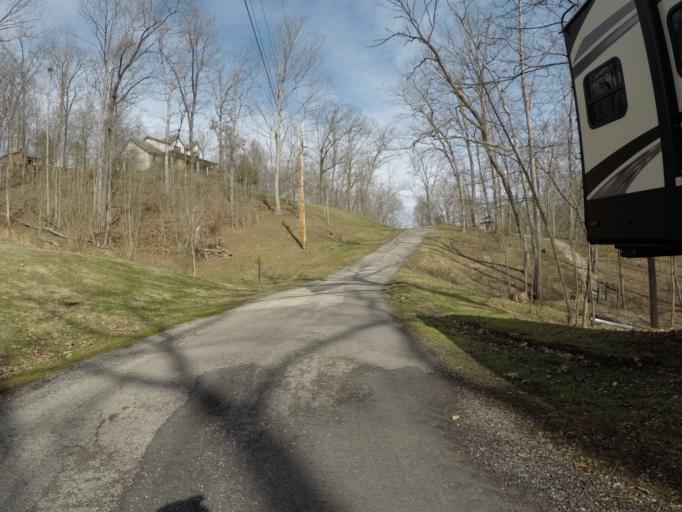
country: US
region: West Virginia
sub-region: Wayne County
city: Ceredo
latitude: 38.3632
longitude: -82.5347
